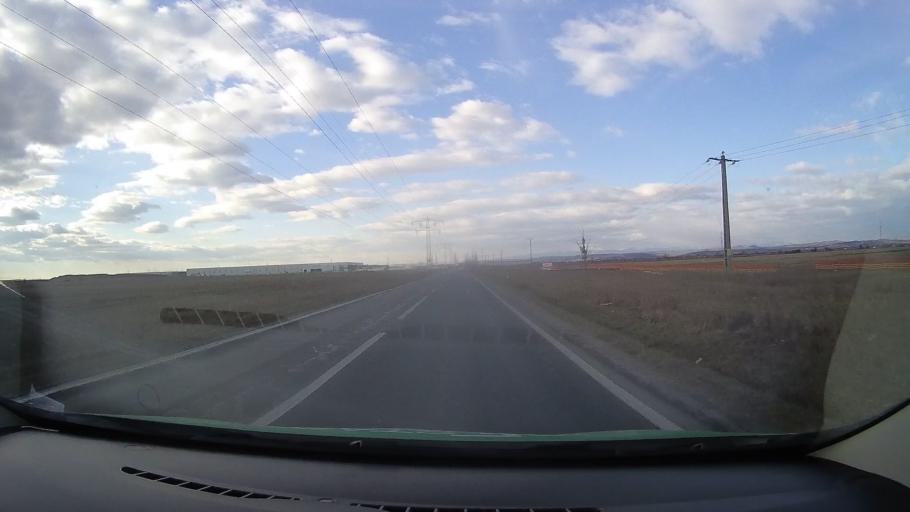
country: RO
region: Dambovita
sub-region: Comuna Comisani
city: Lazuri
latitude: 44.8701
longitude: 25.5243
